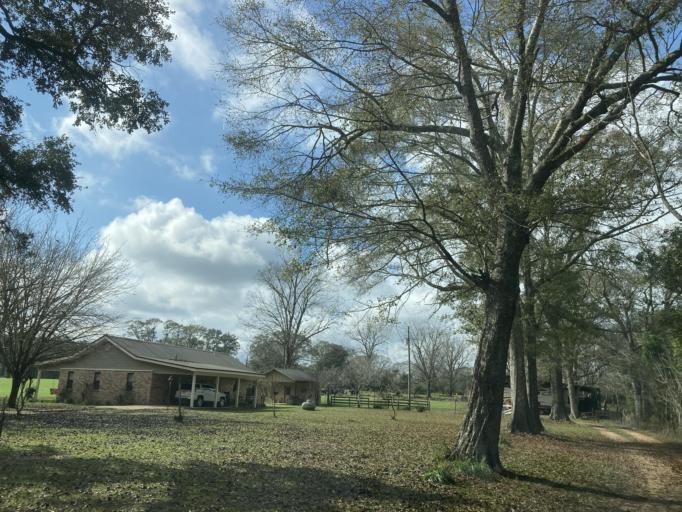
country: US
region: Mississippi
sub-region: Stone County
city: Wiggins
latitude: 30.8579
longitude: -89.3242
